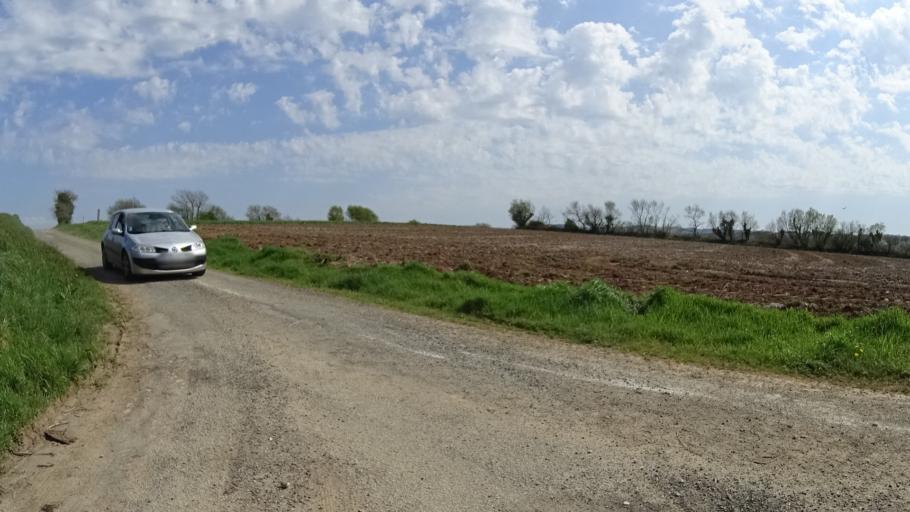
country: FR
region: Brittany
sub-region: Departement du Finistere
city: Sizun
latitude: 48.4175
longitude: -4.0886
